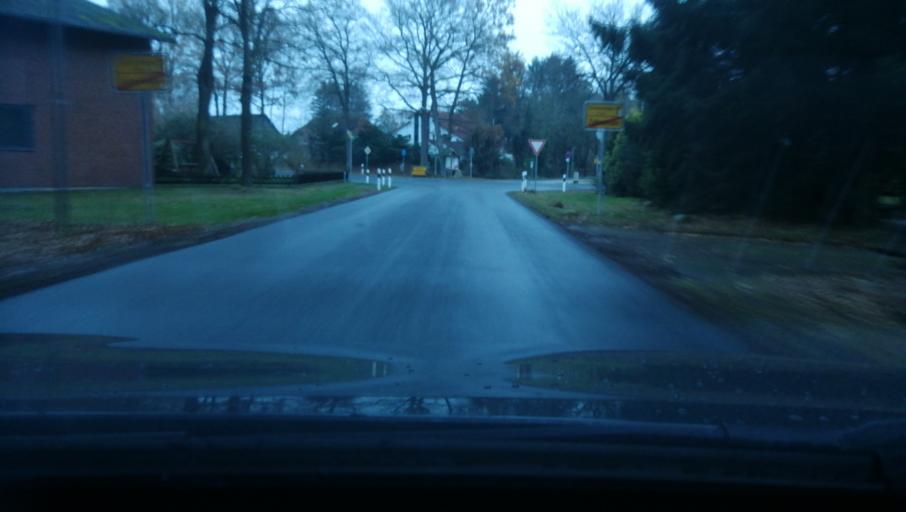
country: DE
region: Lower Saxony
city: Schneverdingen
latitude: 53.1166
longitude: 9.7599
